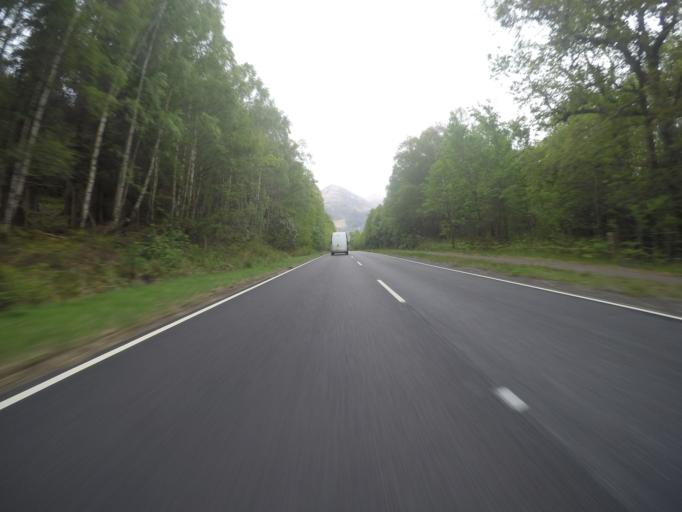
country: GB
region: Scotland
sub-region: Highland
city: Fort William
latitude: 57.2377
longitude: -5.4381
